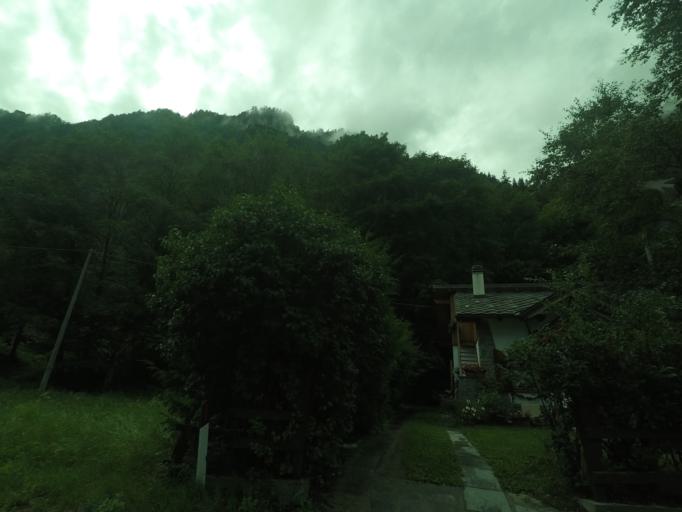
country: IT
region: Aosta Valley
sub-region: Valle d'Aosta
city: Antey-Saint-Andre
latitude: 45.8187
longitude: 7.5885
